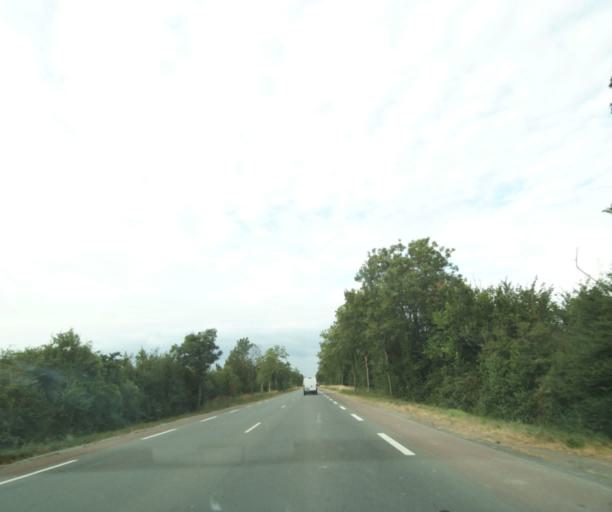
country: FR
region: Poitou-Charentes
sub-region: Departement de la Charente-Maritime
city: Marans
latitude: 46.2791
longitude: -0.9975
